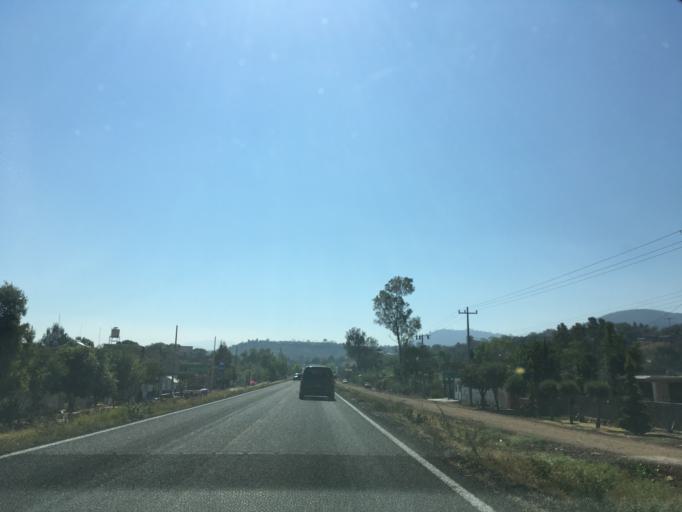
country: MX
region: Michoacan
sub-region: Indaparapeo
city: San Lucas Pio
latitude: 19.7946
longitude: -100.9325
